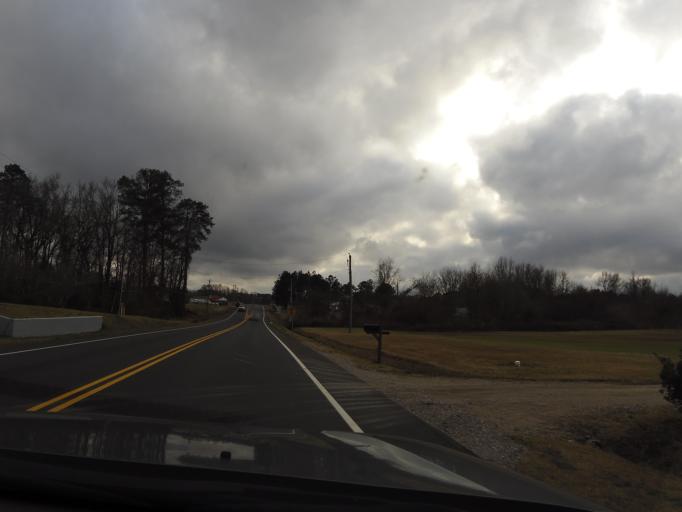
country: US
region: North Carolina
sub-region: Nash County
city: Rocky Mount
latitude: 35.8825
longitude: -77.7411
